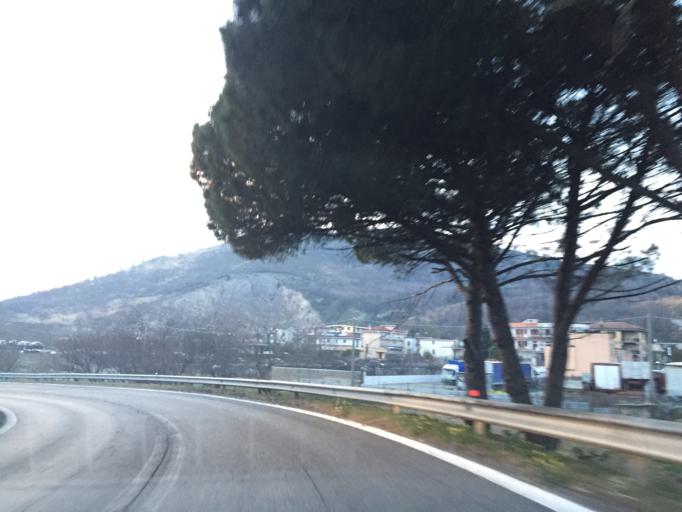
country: IT
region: Campania
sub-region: Provincia di Salerno
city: Lanzara
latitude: 40.7720
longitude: 14.6677
